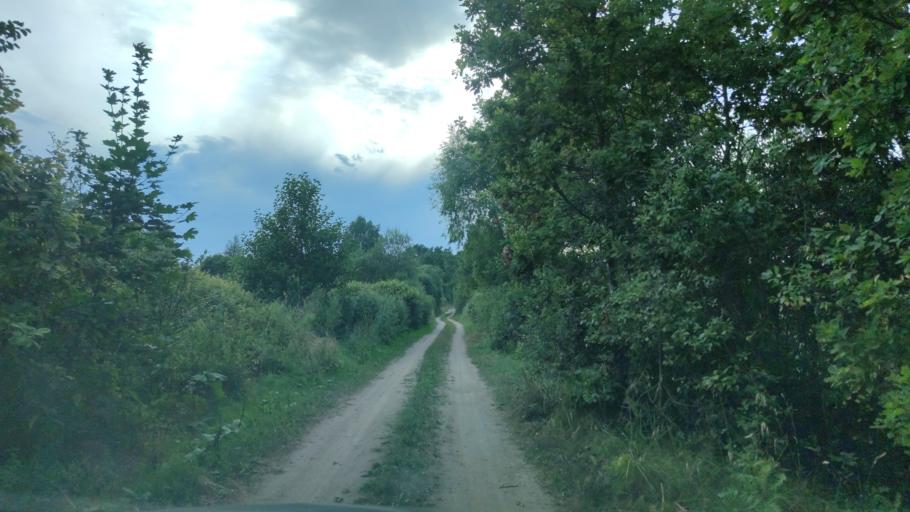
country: BY
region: Vitebsk
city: Mosar
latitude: 55.1226
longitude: 27.1818
